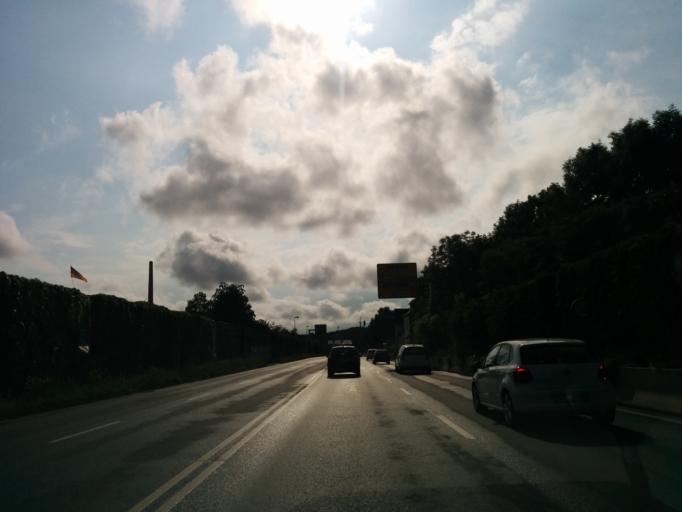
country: DE
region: Lower Saxony
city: Herzberg am Harz
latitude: 51.6510
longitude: 10.3386
